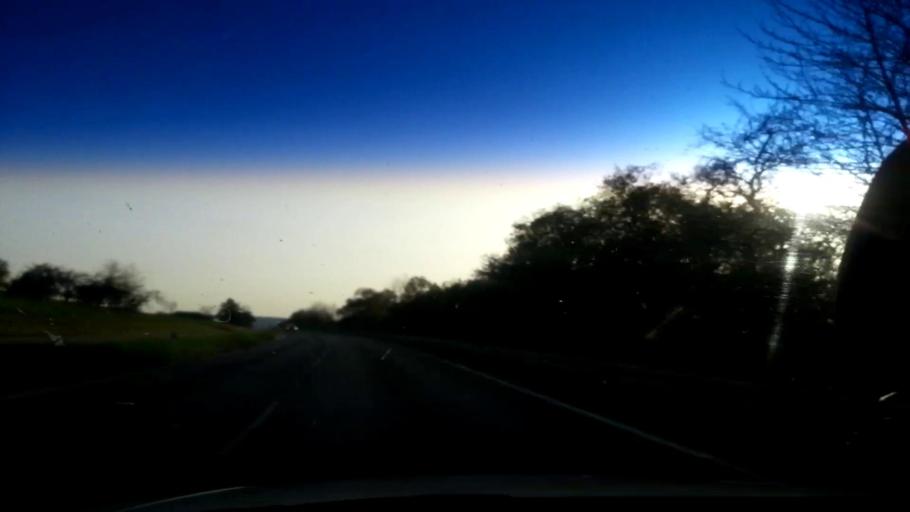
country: DE
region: Bavaria
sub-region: Upper Franconia
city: Zapfendorf
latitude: 50.0345
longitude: 10.9420
